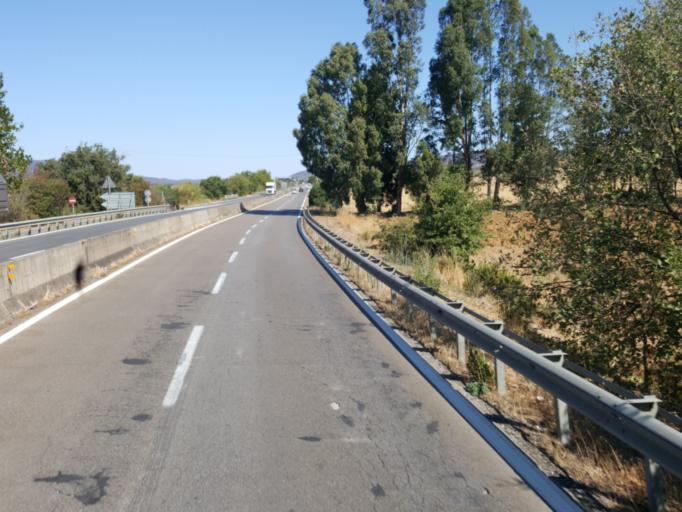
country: IT
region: Tuscany
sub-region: Provincia di Grosseto
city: Fonteblanda
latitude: 42.5709
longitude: 11.1682
